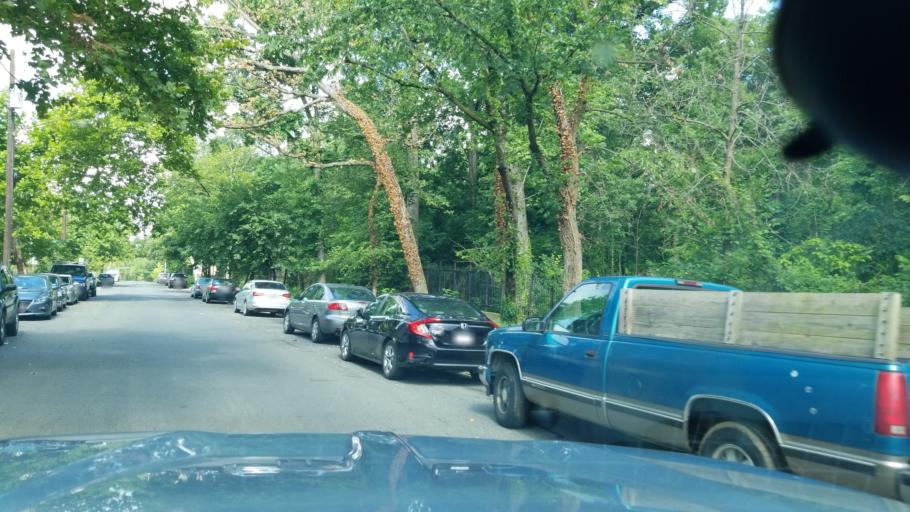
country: US
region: Maryland
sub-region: Prince George's County
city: Mount Rainier
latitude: 38.9056
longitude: -76.9733
